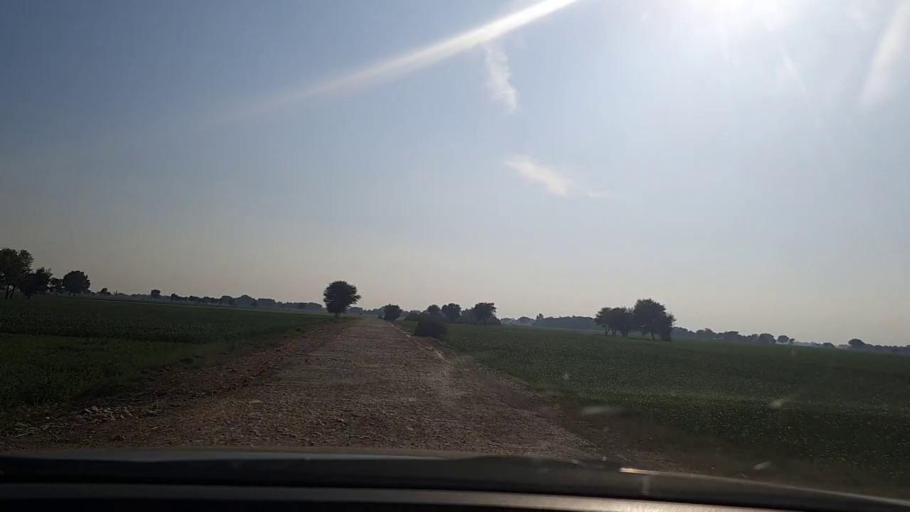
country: PK
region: Sindh
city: Sehwan
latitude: 26.3149
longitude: 68.0036
